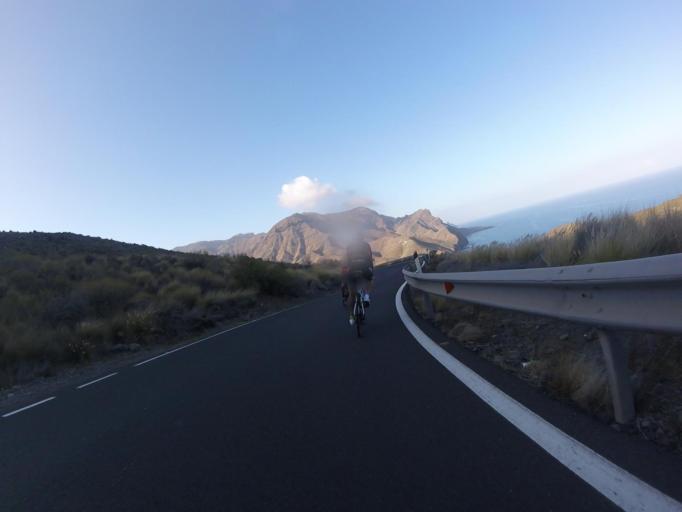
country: ES
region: Canary Islands
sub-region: Provincia de Las Palmas
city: Agaete
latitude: 28.0594
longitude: -15.7297
